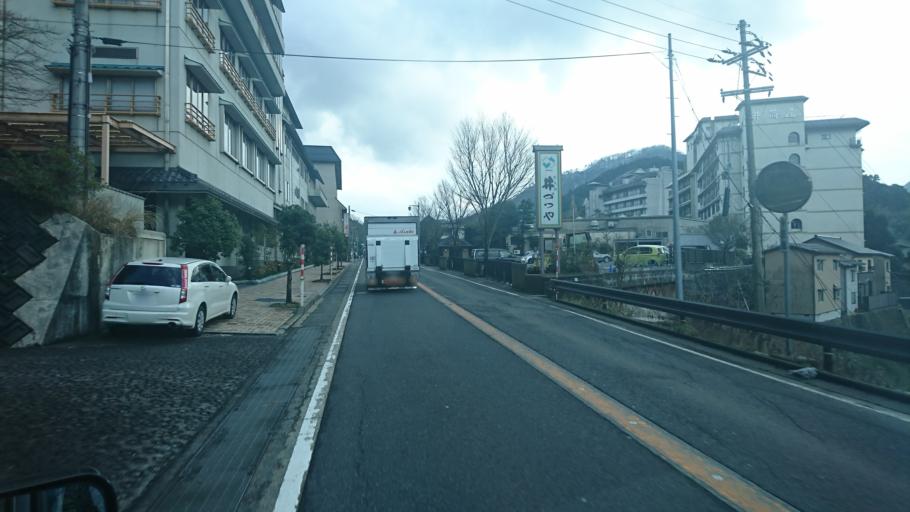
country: JP
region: Tottori
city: Tottori
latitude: 35.5571
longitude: 134.4885
